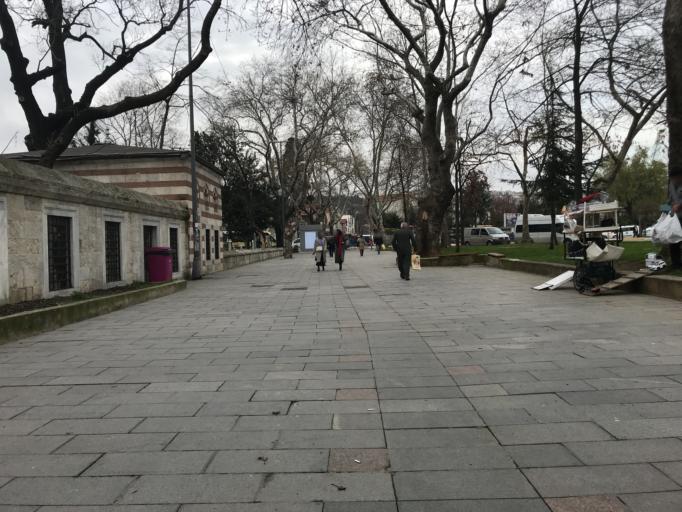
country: TR
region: Istanbul
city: Istanbul
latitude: 41.0452
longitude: 28.9362
